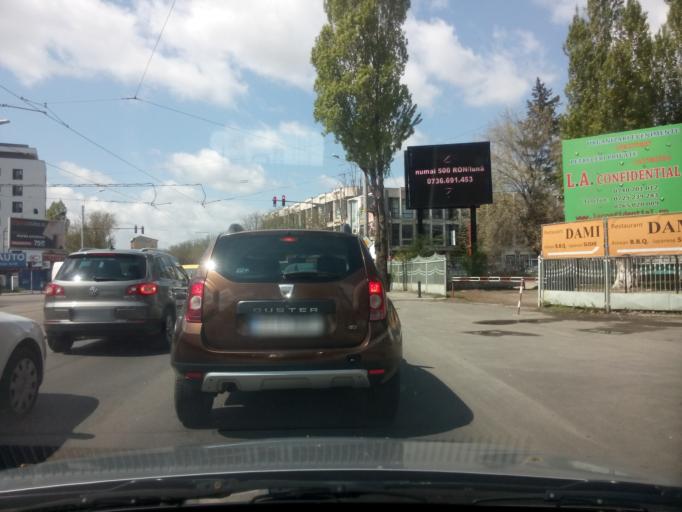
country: RO
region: Ilfov
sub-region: Comuna Otopeni
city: Otopeni
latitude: 44.4935
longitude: 26.0864
